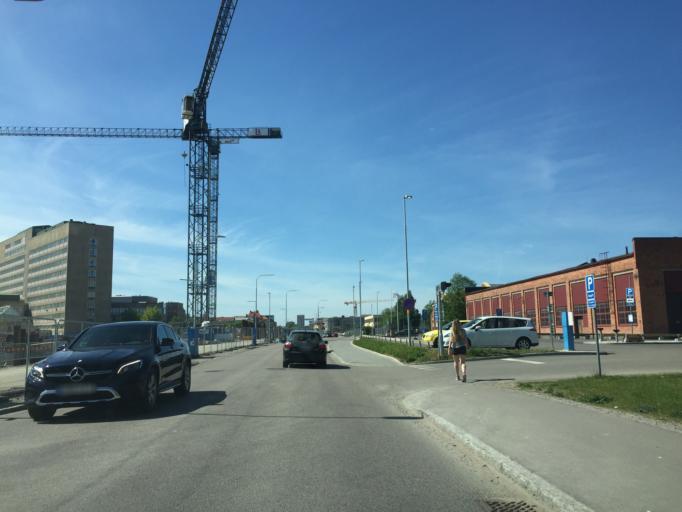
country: SE
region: OErebro
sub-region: Orebro Kommun
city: Orebro
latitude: 59.2758
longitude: 15.2317
